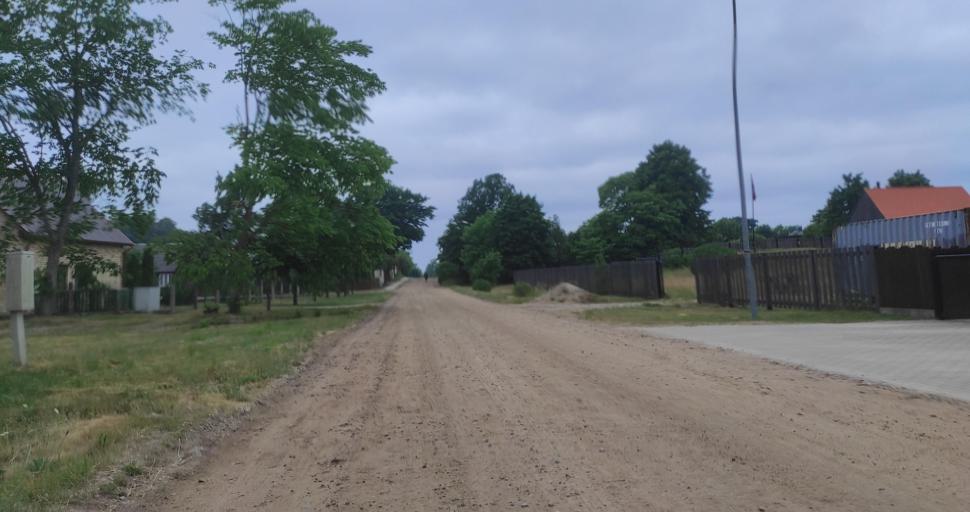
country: LV
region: Pavilostas
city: Pavilosta
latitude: 56.8890
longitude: 21.1875
